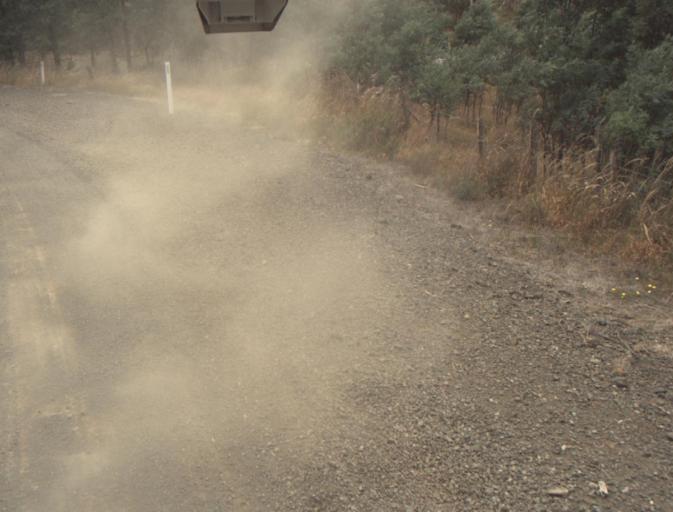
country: AU
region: Tasmania
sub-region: Northern Midlands
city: Evandale
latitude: -41.5193
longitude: 147.3818
